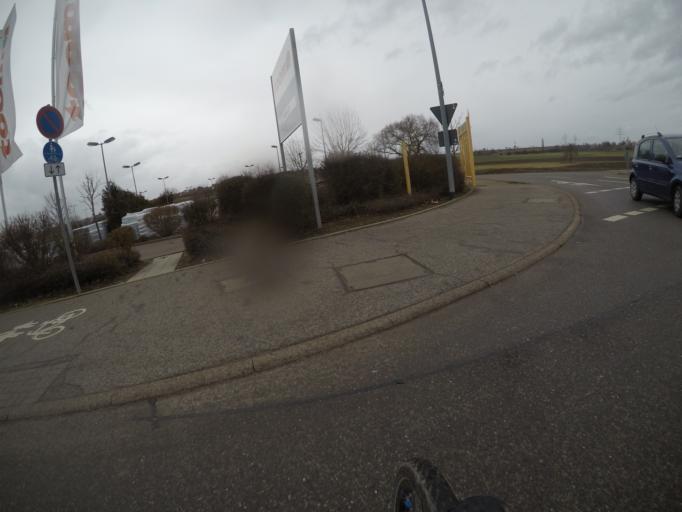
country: DE
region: Baden-Wuerttemberg
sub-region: Regierungsbezirk Stuttgart
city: Herrenberg
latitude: 48.6045
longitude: 8.8715
